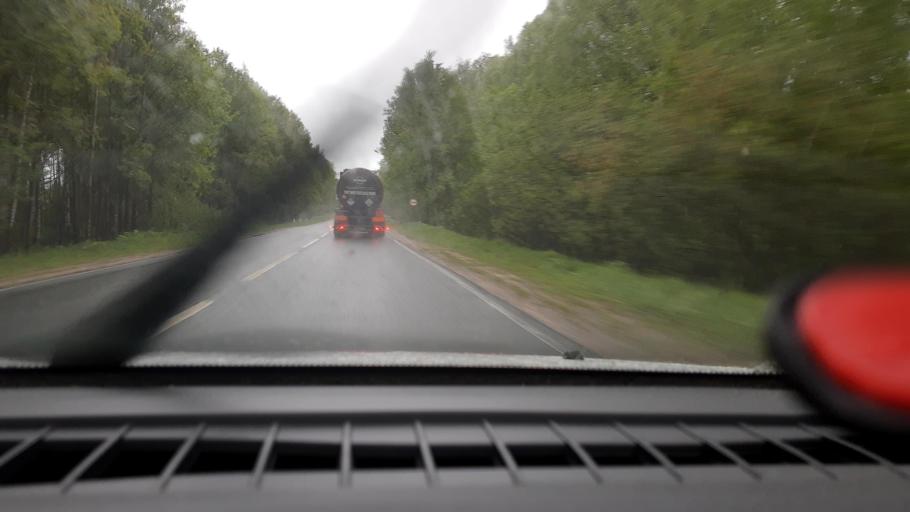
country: RU
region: Nizjnij Novgorod
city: Sukhobezvodnoye
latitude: 56.8622
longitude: 44.8992
